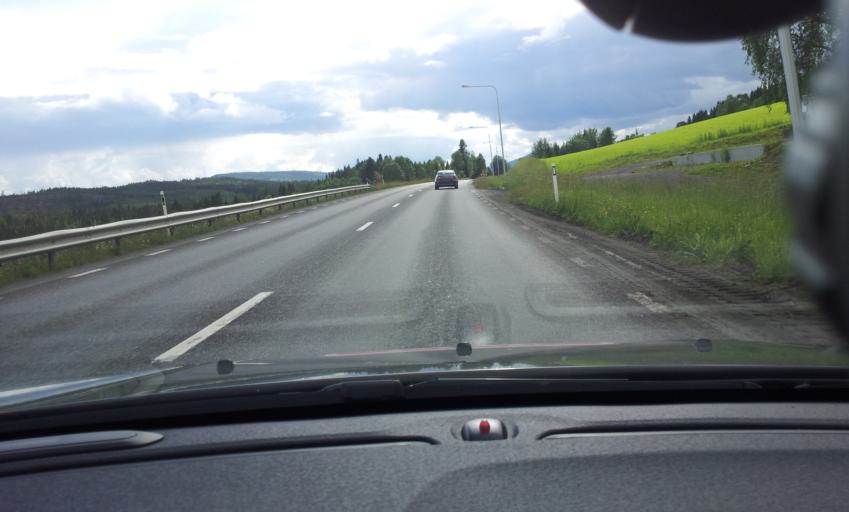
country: SE
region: Jaemtland
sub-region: Are Kommun
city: Jarpen
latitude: 63.3313
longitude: 13.4082
